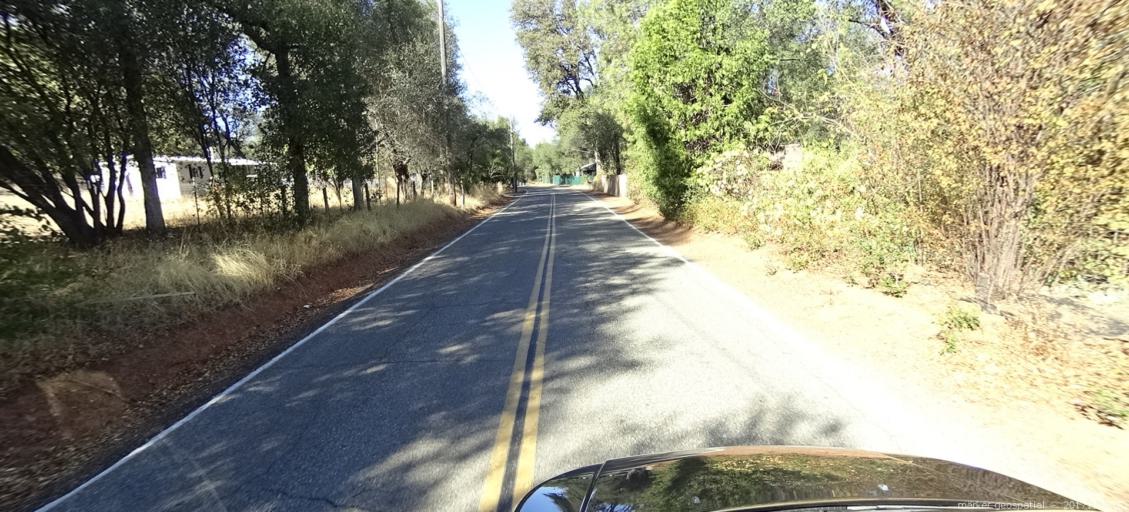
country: US
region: California
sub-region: Shasta County
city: Palo Cedro
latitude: 40.5777
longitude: -122.2996
